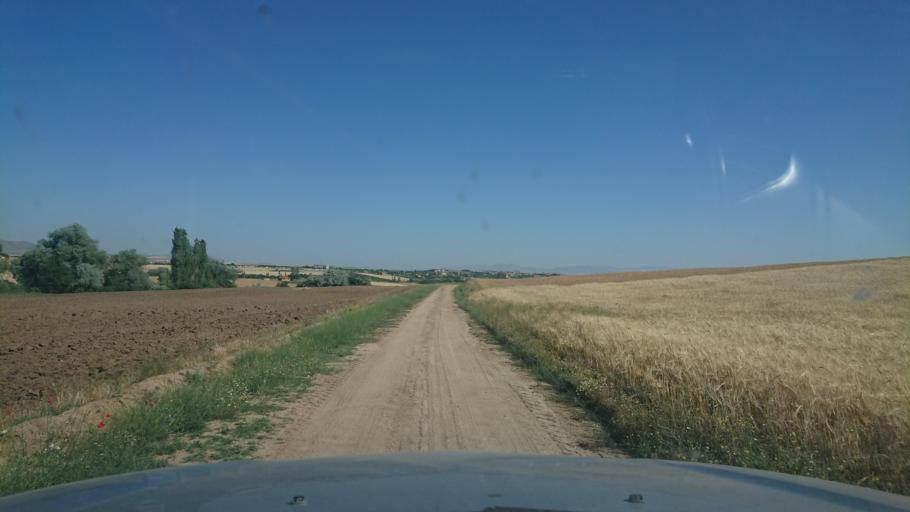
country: TR
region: Aksaray
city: Agacoren
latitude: 38.8513
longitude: 33.9151
